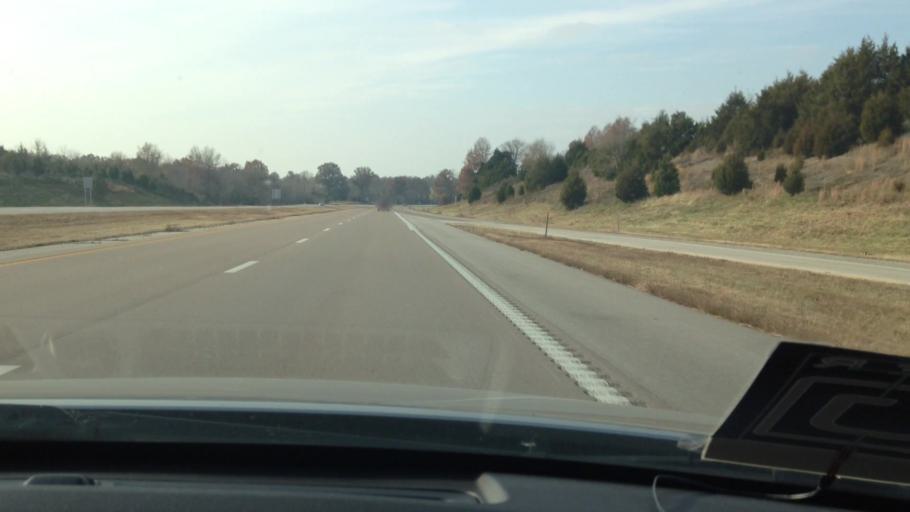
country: US
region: Missouri
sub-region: Cass County
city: Garden City
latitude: 38.4677
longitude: -94.0052
